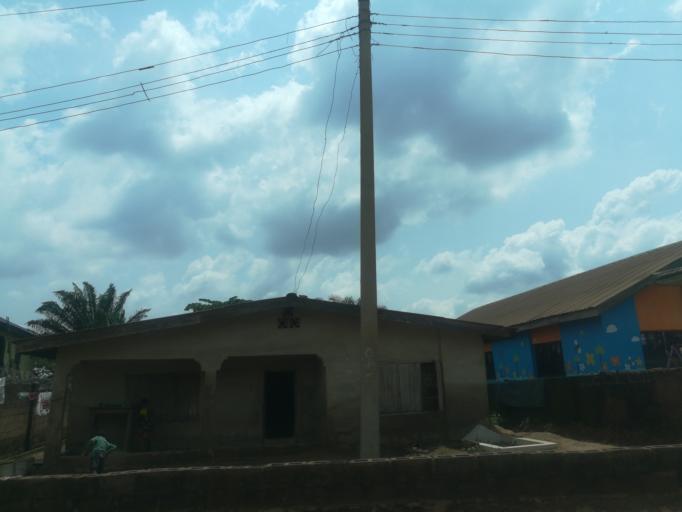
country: NG
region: Oyo
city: Ibadan
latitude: 7.4507
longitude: 3.9551
